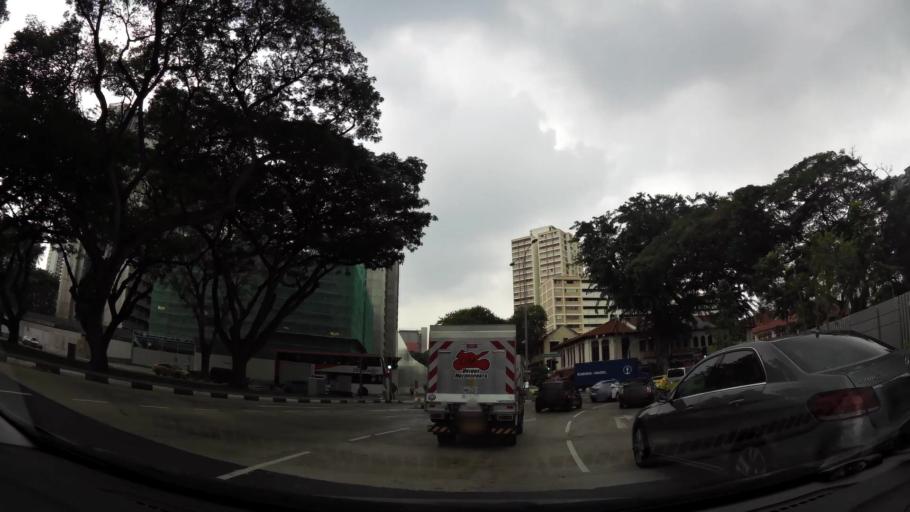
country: SG
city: Singapore
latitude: 1.3217
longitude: 103.8637
